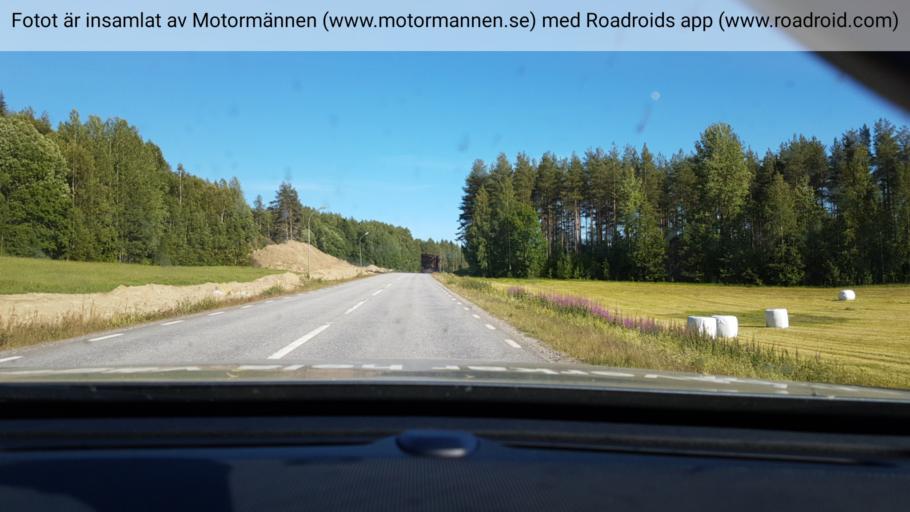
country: SE
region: Vaesterbotten
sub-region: Bjurholms Kommun
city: Bjurholm
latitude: 64.2401
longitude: 19.3347
